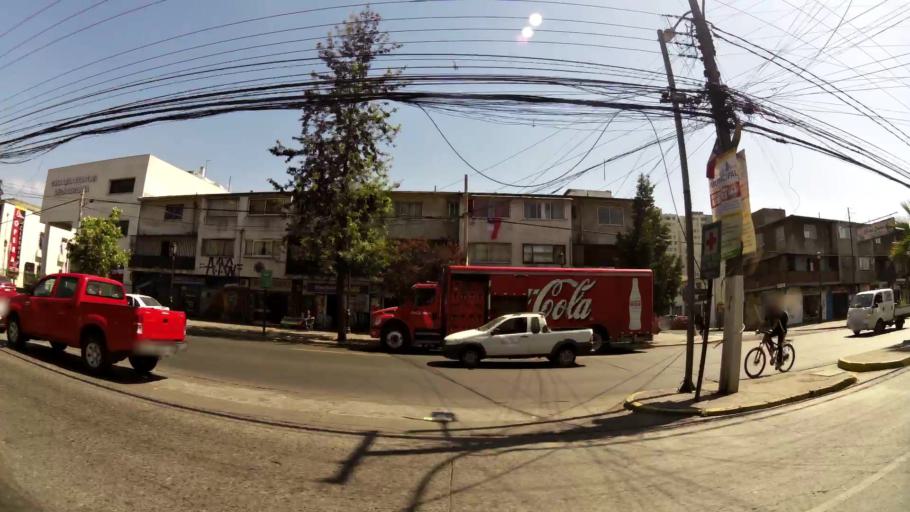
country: CL
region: Santiago Metropolitan
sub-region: Provincia de Santiago
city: La Pintana
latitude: -33.5344
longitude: -70.6636
